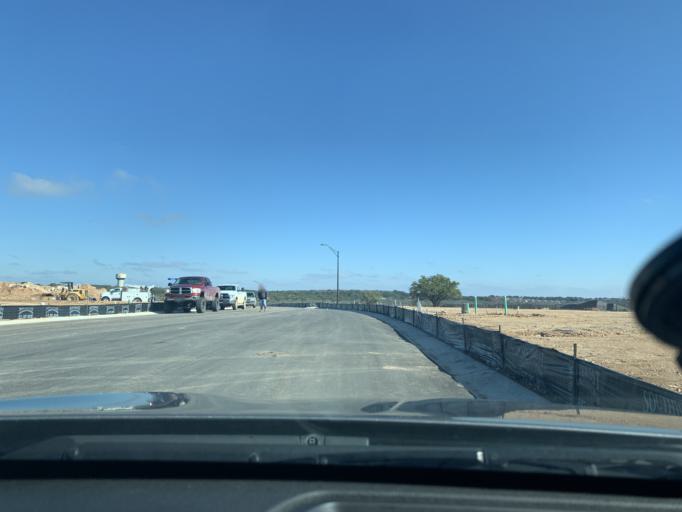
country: US
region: Texas
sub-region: Williamson County
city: Serenada
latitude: 30.7334
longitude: -97.7618
